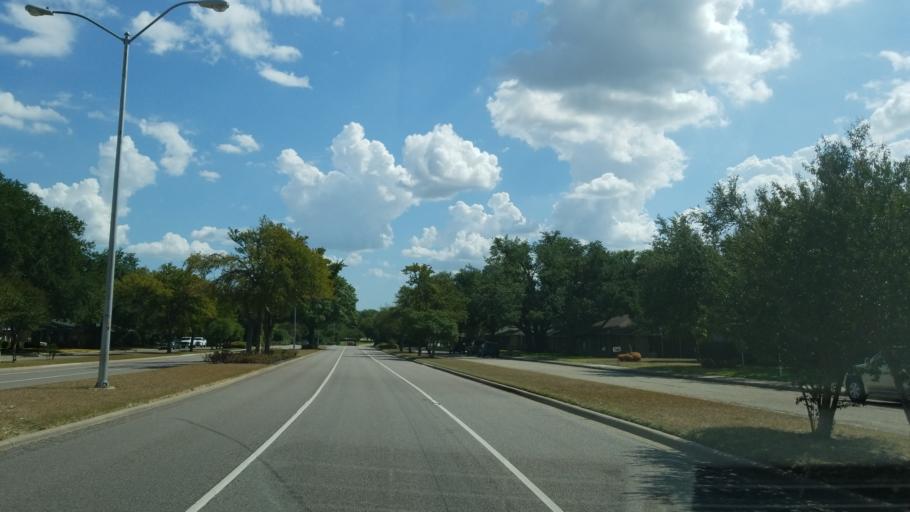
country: US
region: Texas
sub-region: Dallas County
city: Addison
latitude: 32.9533
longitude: -96.7865
